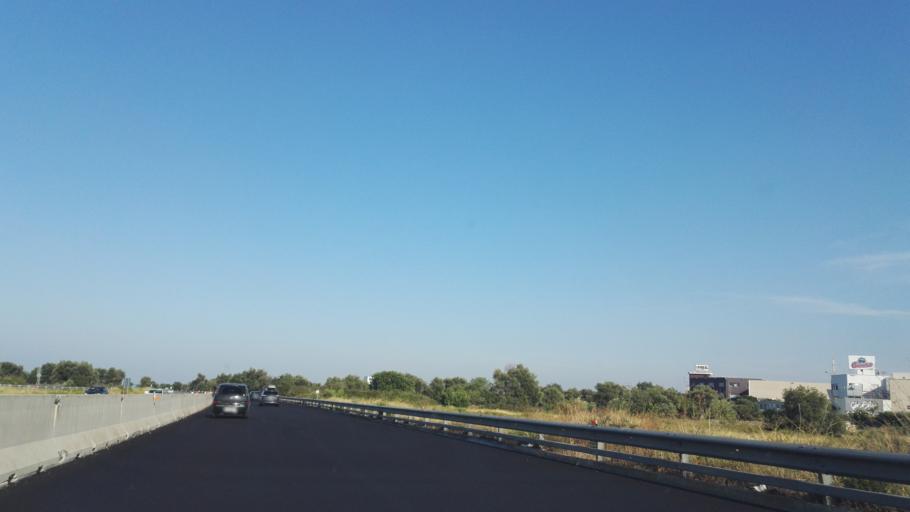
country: IT
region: Apulia
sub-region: Provincia di Brindisi
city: Pezze di Greco
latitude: 40.8346
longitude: 17.3917
